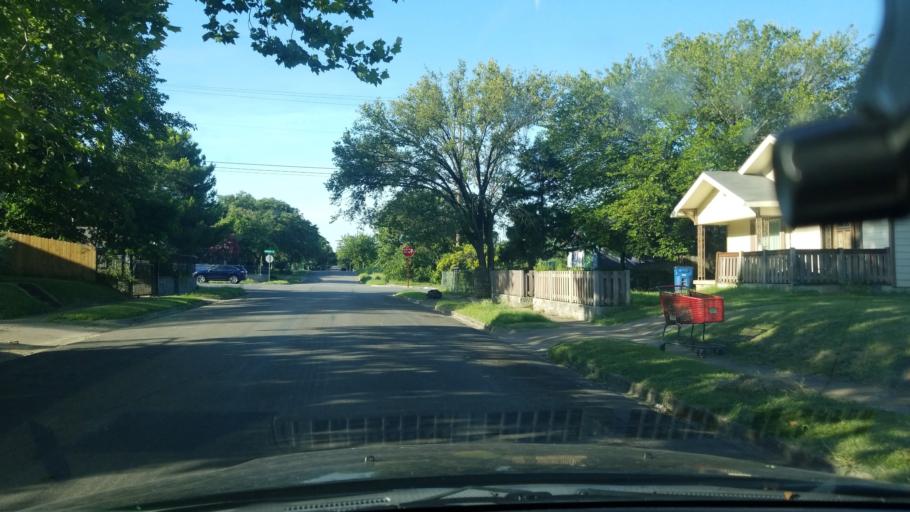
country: US
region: Texas
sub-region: Dallas County
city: Dallas
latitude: 32.7209
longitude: -96.8170
